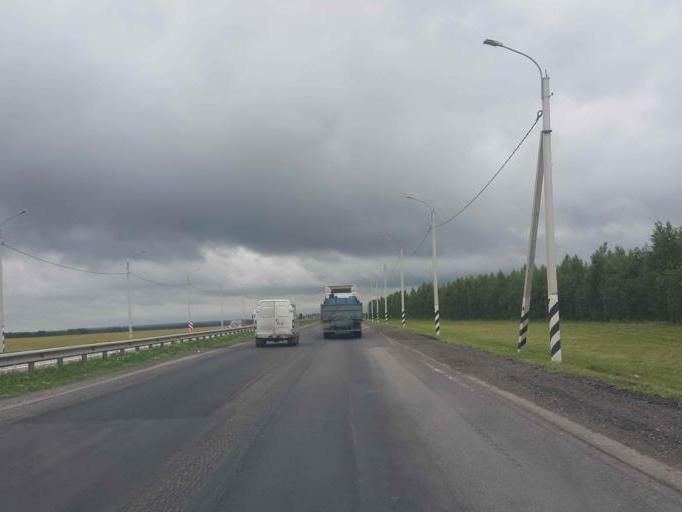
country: RU
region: Tambov
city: Selezni
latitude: 52.7401
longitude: 41.2274
